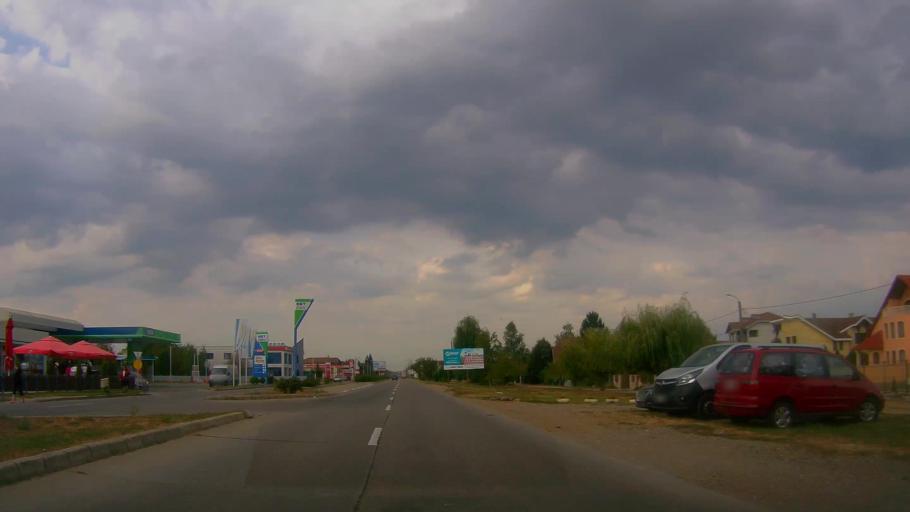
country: RO
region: Satu Mare
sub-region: Comuna Paulesti
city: Paulesti
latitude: 47.8082
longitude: 22.9165
